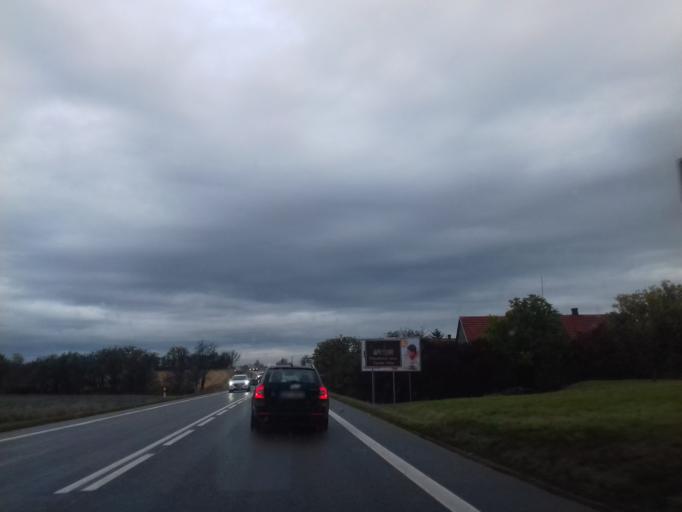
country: CZ
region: Pardubicky
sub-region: Okres Pardubice
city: Vysoke Myto
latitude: 49.9156
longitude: 16.1944
